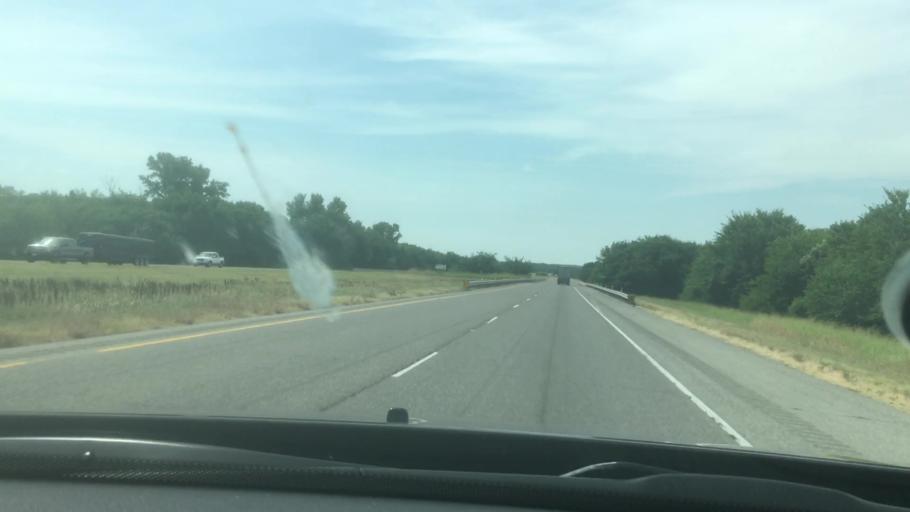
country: US
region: Oklahoma
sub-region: Murray County
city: Davis
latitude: 34.5356
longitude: -97.1882
